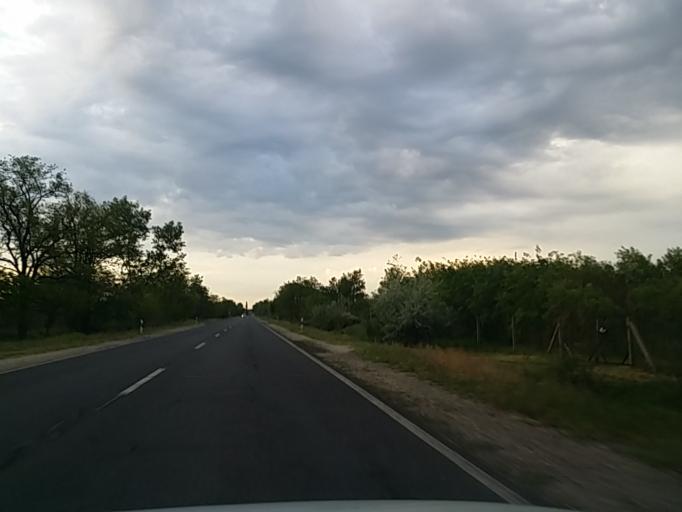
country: HU
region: Pest
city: Taborfalva
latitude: 47.0761
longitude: 19.4922
